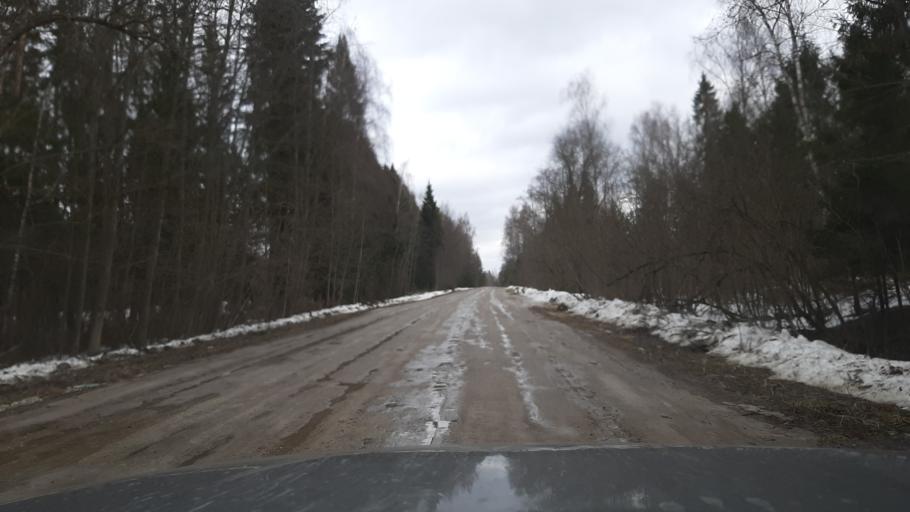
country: RU
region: Ivanovo
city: Teykovo
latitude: 56.8880
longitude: 40.6561
